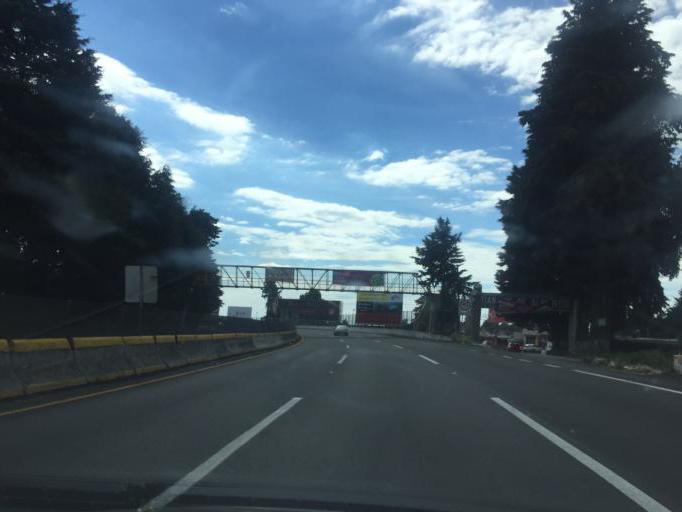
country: MX
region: Morelos
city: Tres Marias
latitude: 19.0502
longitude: -99.2409
